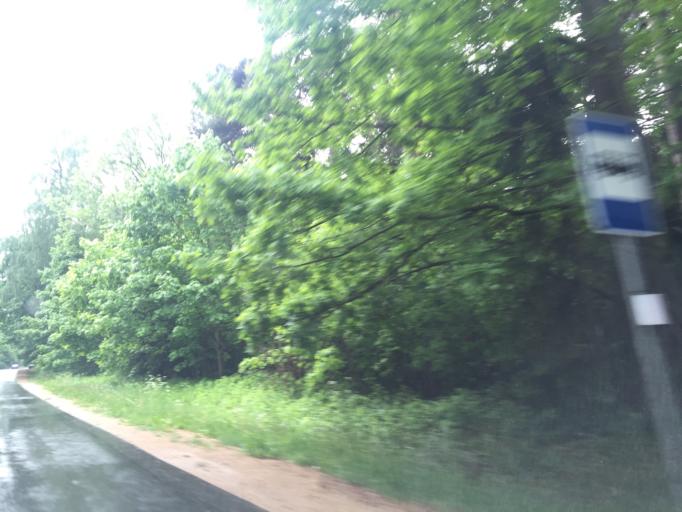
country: LT
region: Klaipedos apskritis
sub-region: Klaipeda
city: Klaipeda
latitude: 55.7816
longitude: 21.0793
